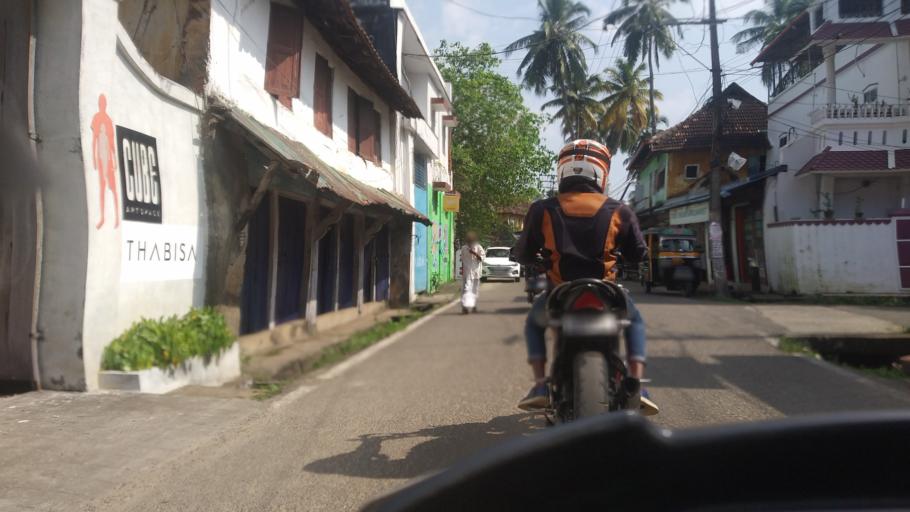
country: IN
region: Kerala
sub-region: Ernakulam
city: Cochin
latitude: 9.9621
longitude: 76.2580
